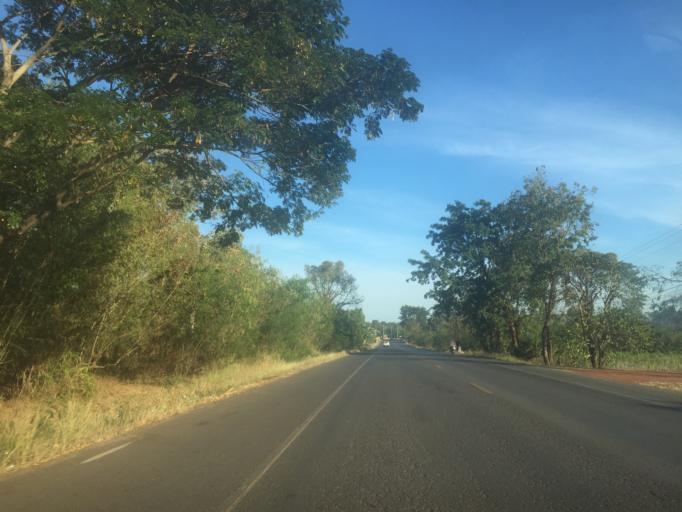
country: TH
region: Changwat Udon Thani
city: Si That
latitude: 16.9705
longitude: 103.2367
